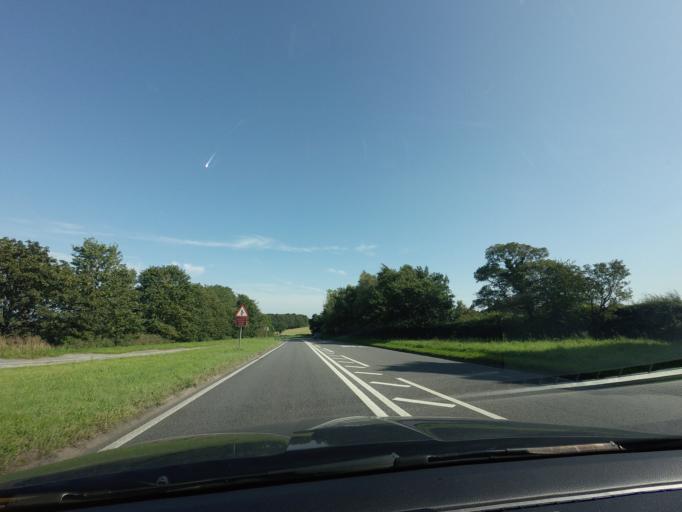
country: GB
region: England
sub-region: Derbyshire
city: Wingerworth
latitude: 53.2304
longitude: -1.5123
